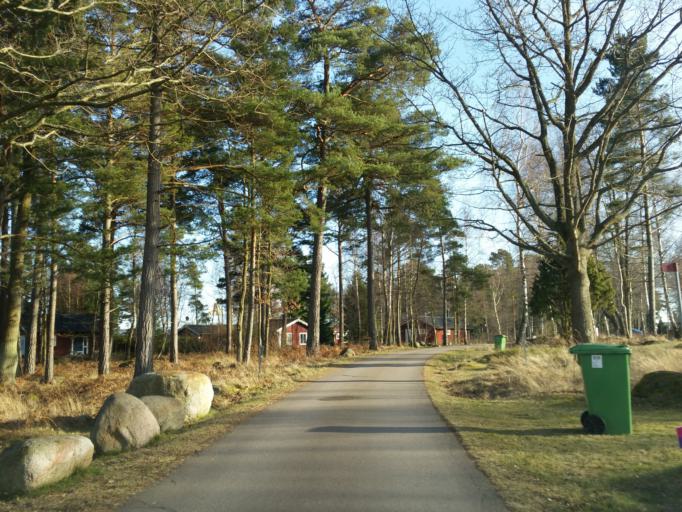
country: SE
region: Kalmar
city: Faerjestaden
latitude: 56.7809
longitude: 16.4785
